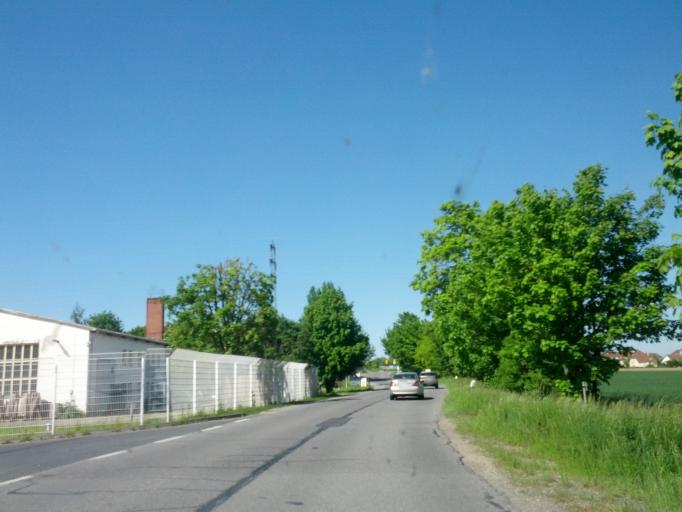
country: DE
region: Saxony
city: Bannewitz
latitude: 51.0007
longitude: 13.7636
